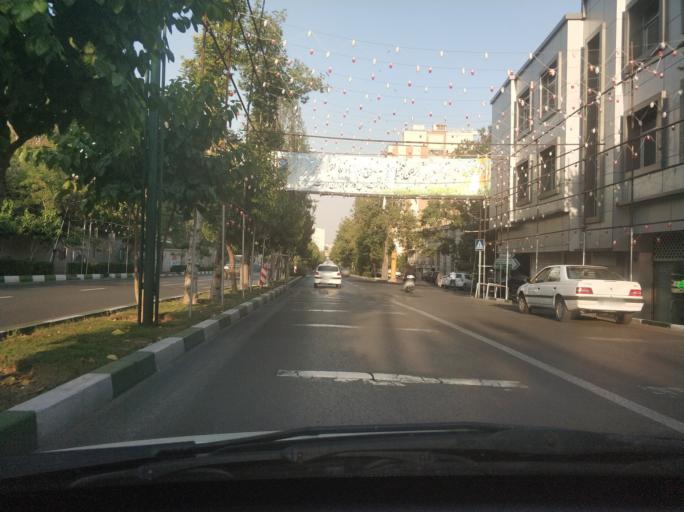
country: IR
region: Tehran
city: Tajrish
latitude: 35.8003
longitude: 51.4670
